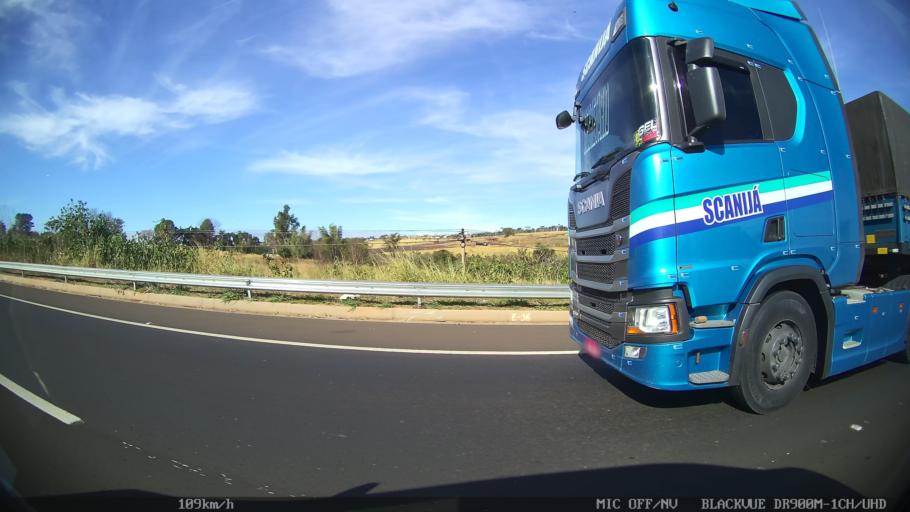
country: BR
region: Sao Paulo
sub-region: Sao Jose Do Rio Preto
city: Sao Jose do Rio Preto
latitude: -20.7521
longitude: -49.3406
